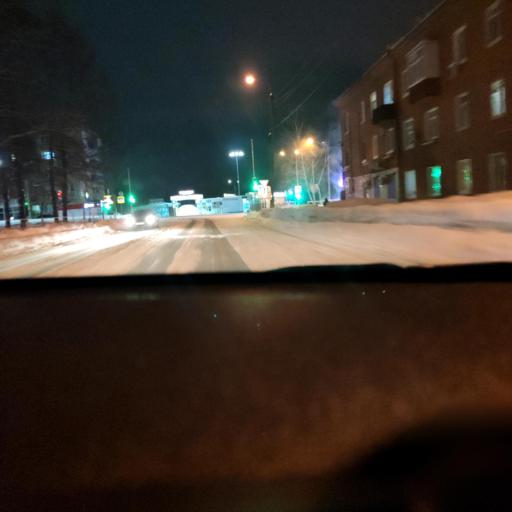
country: RU
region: Tatarstan
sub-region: Chistopol'skiy Rayon
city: Chistopol'
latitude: 55.3655
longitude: 50.6082
